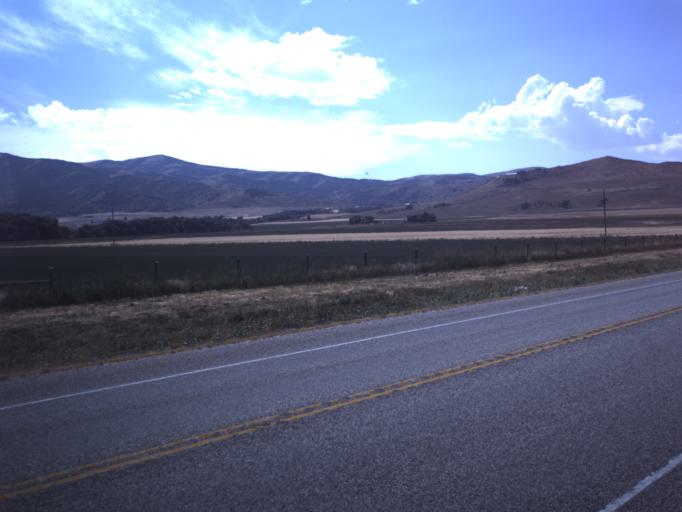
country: US
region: Utah
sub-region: Cache County
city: Mendon
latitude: 41.7525
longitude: -111.9865
